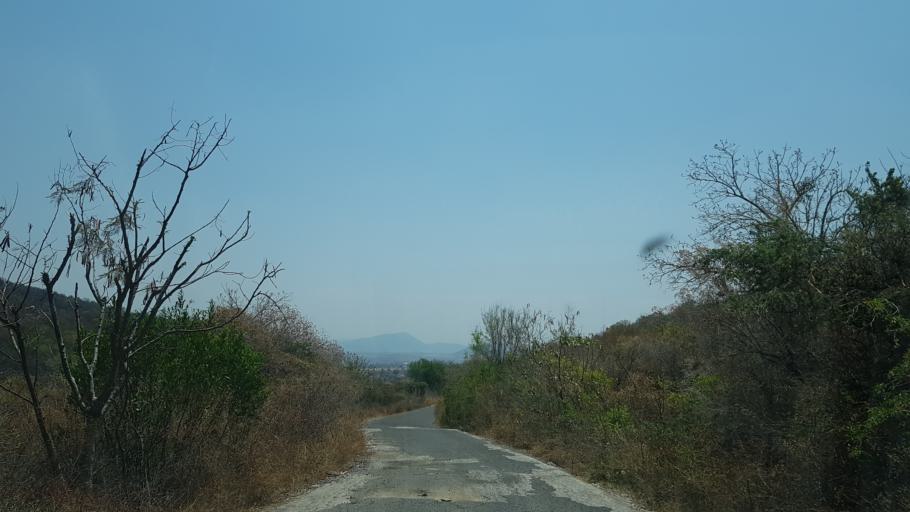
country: MX
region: Puebla
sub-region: Atzitzihuacan
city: San Miguel Aguacomulican
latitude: 18.7955
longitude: -98.5462
